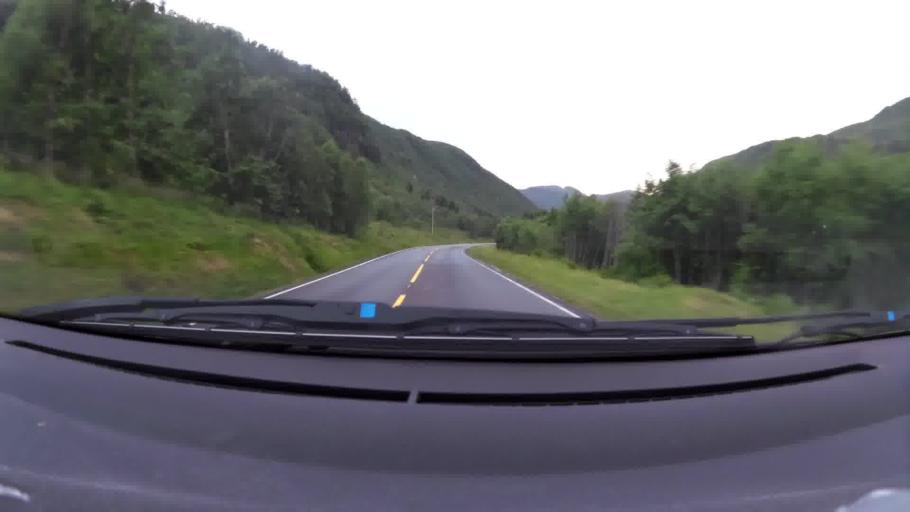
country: NO
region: More og Romsdal
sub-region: Molde
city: Molde
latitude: 62.7996
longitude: 7.3123
